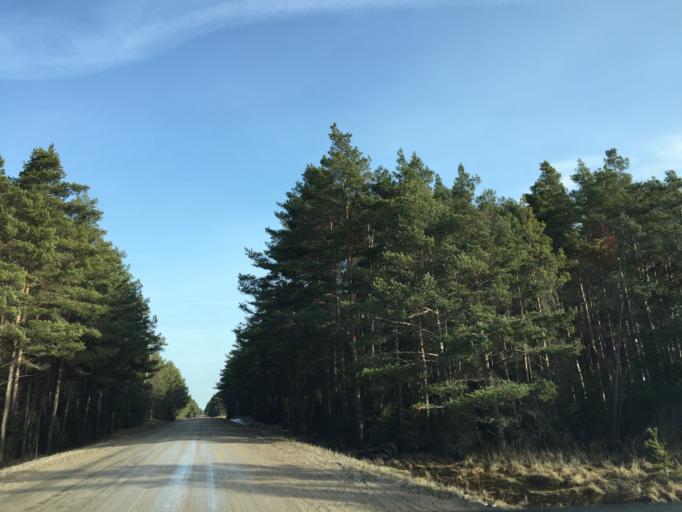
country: EE
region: Saare
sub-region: Kuressaare linn
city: Kuressaare
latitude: 58.2991
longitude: 21.9545
